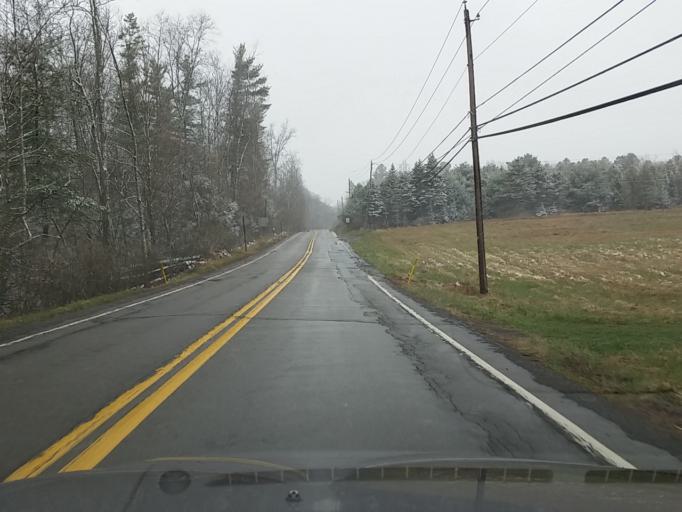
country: US
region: Pennsylvania
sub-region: Luzerne County
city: East Berwick
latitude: 41.1965
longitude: -76.2498
